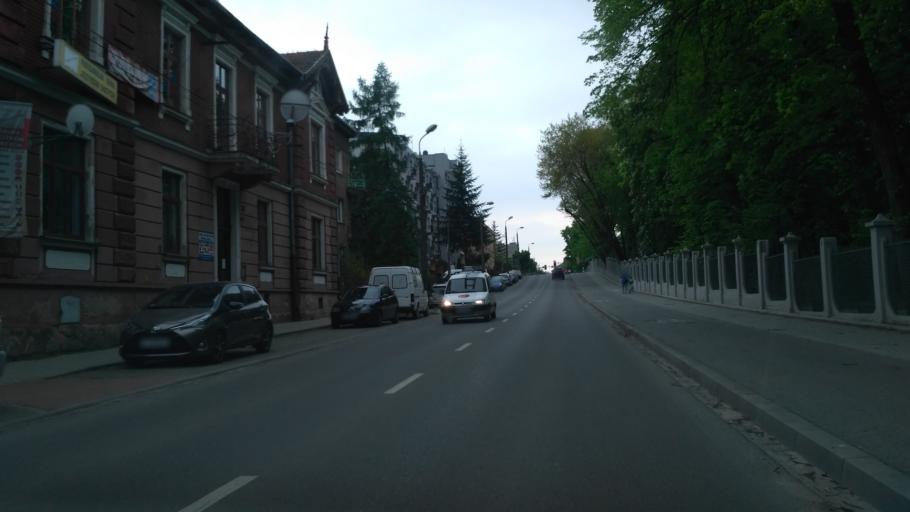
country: PL
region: Lesser Poland Voivodeship
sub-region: Powiat tarnowski
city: Tarnow
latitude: 50.0197
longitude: 20.9870
